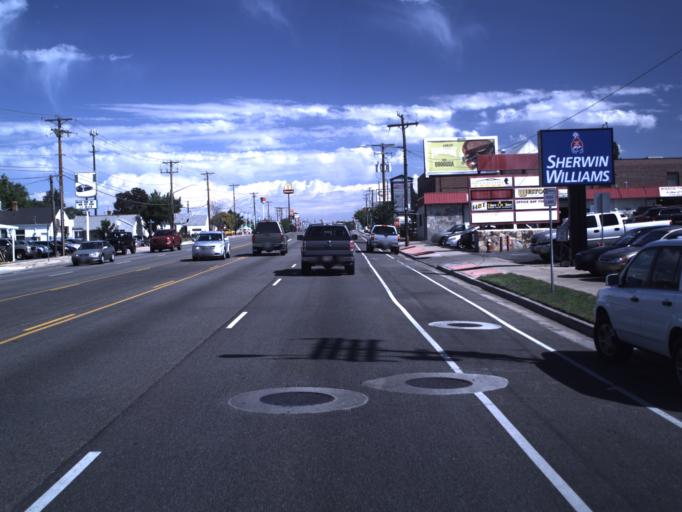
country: US
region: Utah
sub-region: Davis County
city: Clearfield
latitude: 41.1192
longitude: -112.0260
